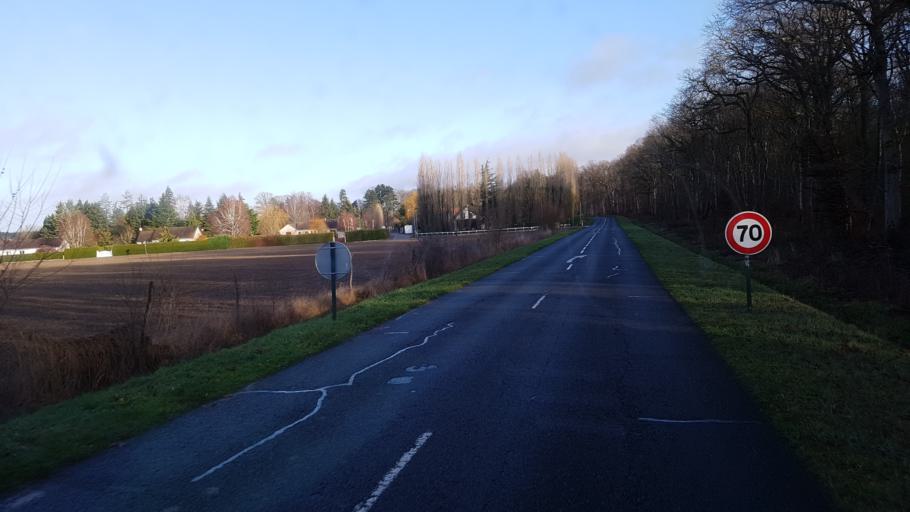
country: FR
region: Centre
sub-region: Departement du Loiret
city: Chilleurs-aux-Bois
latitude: 48.0614
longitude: 2.2246
